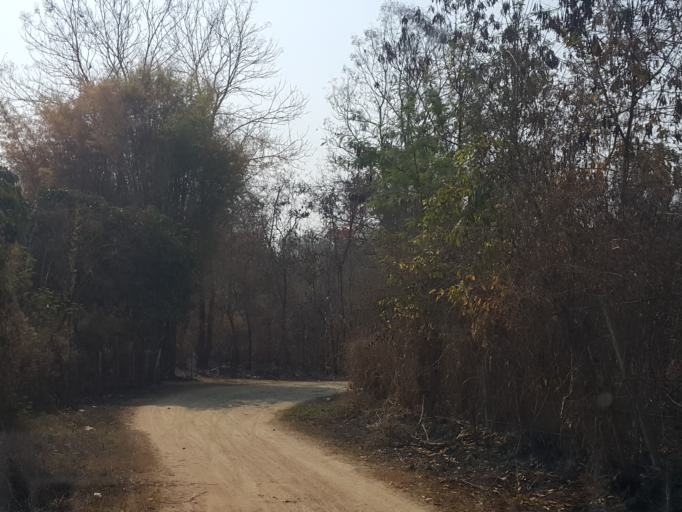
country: TH
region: Chiang Mai
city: Hang Dong
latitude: 18.7143
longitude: 98.8538
